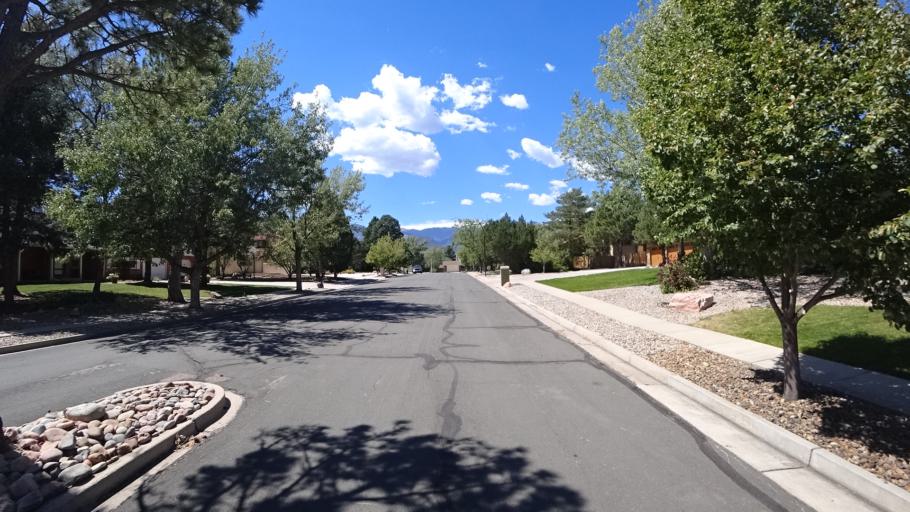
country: US
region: Colorado
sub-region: El Paso County
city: Colorado Springs
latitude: 38.7891
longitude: -104.8276
